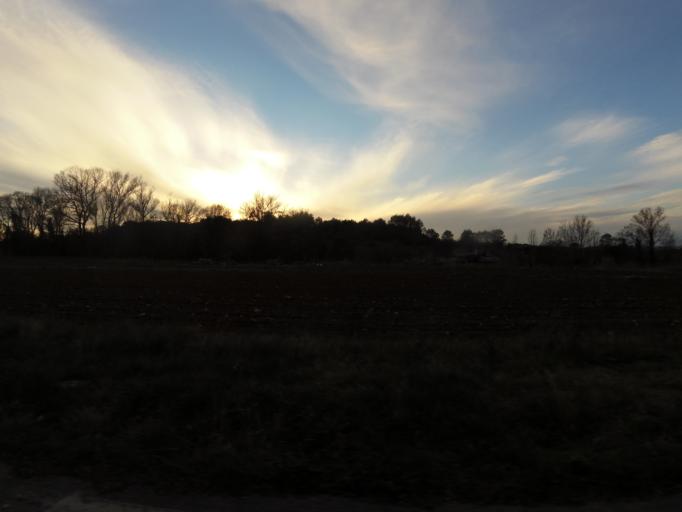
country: FR
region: Languedoc-Roussillon
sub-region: Departement du Gard
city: Saint-Mamert-du-Gard
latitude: 43.8670
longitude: 4.2142
